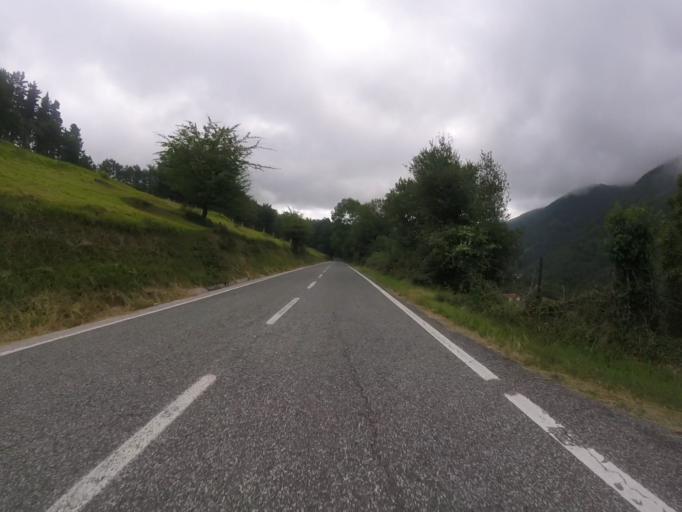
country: ES
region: Navarre
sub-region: Provincia de Navarra
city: Ezkurra
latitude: 43.0851
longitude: -1.8481
